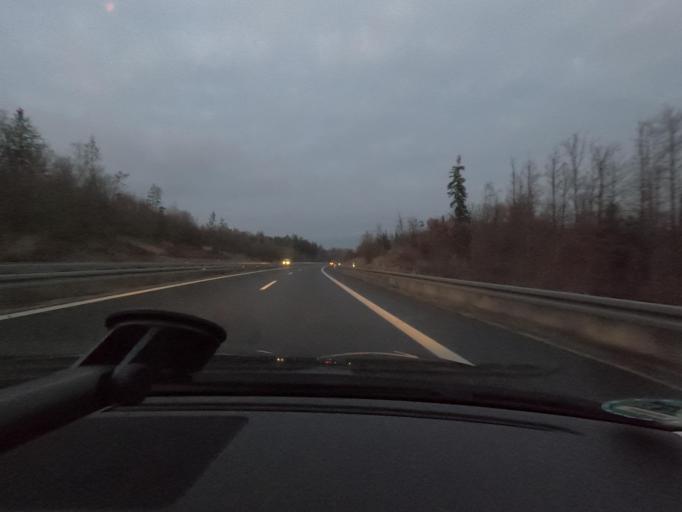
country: DE
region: Bavaria
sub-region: Upper Franconia
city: Untersiemau
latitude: 50.1722
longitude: 11.0086
